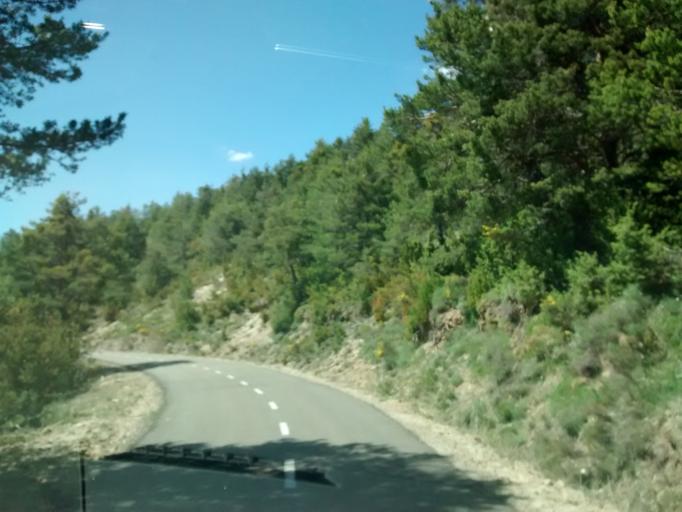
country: ES
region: Aragon
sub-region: Provincia de Huesca
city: Borau
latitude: 42.6726
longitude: -0.6088
